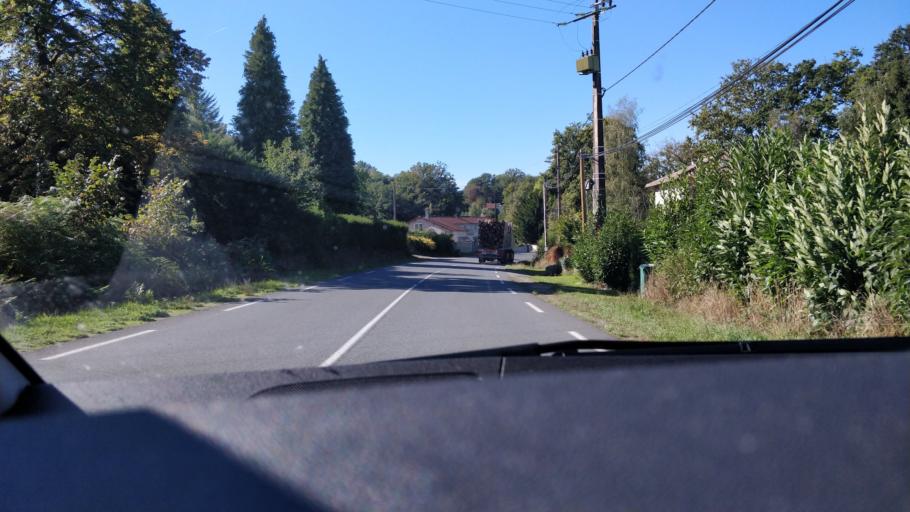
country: FR
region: Limousin
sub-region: Departement de la Haute-Vienne
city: Saint-Just-le-Martel
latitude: 45.8471
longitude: 1.4253
